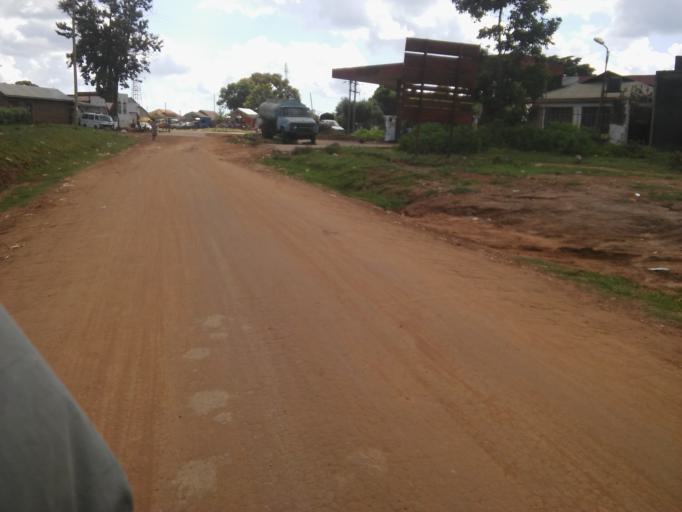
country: UG
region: Eastern Region
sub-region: Pallisa District
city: Pallisa
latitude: 1.1670
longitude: 33.7127
